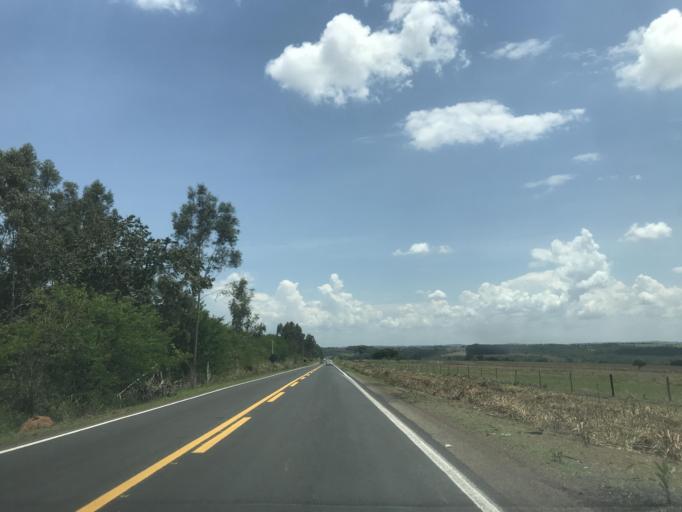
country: BR
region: Goias
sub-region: Bela Vista De Goias
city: Bela Vista de Goias
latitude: -17.1068
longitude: -48.6653
